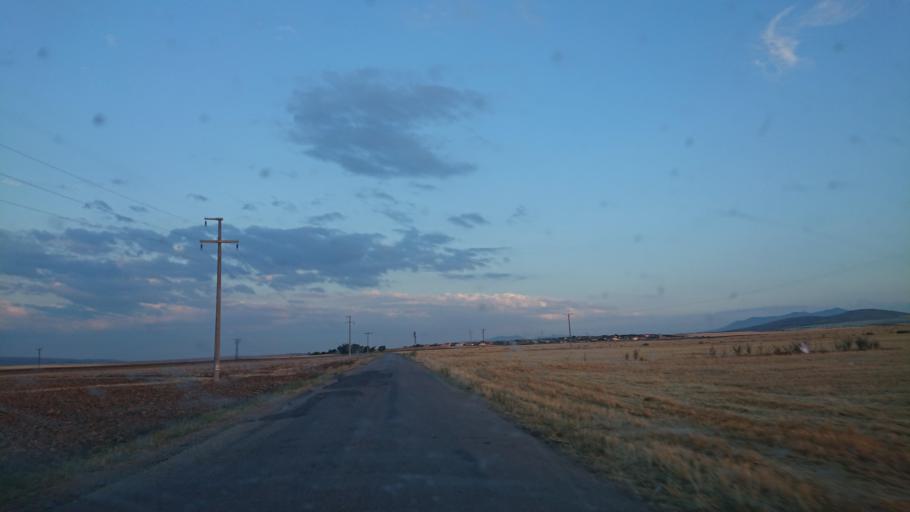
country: TR
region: Aksaray
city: Ortakoy
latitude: 38.8396
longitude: 34.0862
